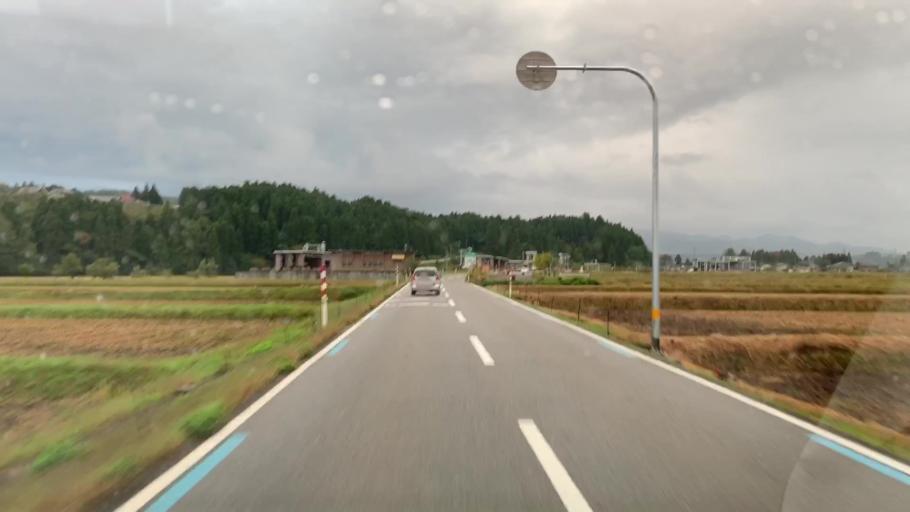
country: JP
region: Toyama
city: Kamiichi
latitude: 36.6218
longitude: 137.3286
